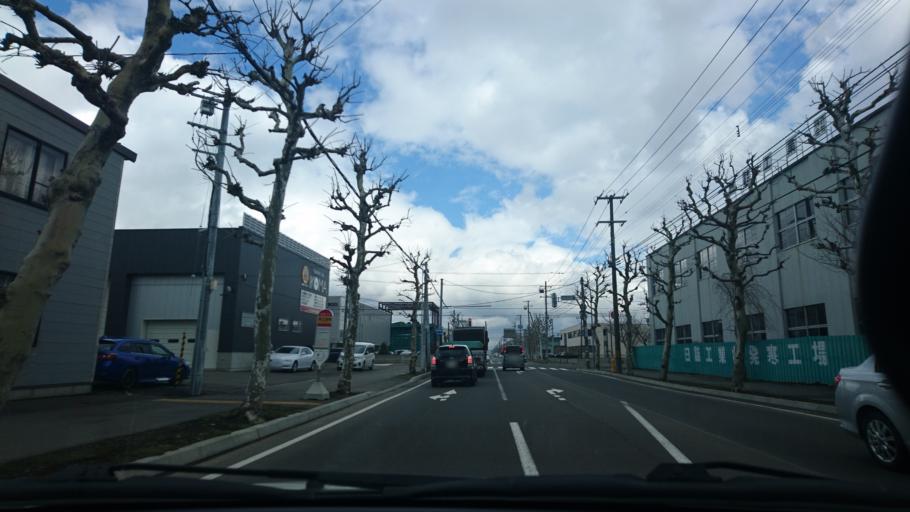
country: JP
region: Hokkaido
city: Sapporo
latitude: 43.1047
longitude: 141.2845
